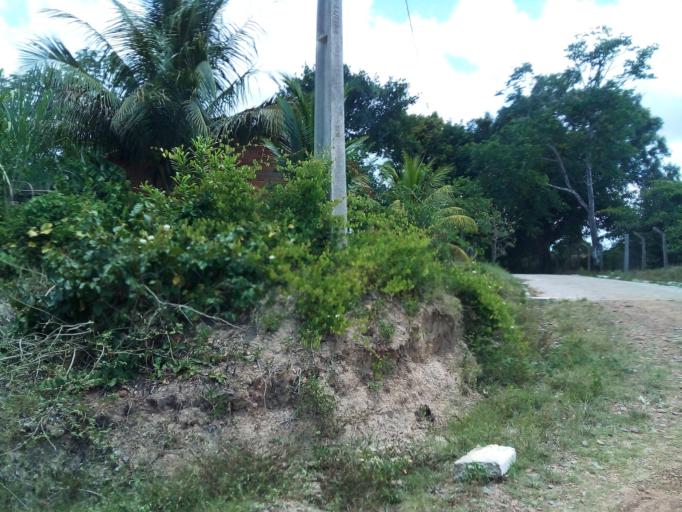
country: BR
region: Maranhao
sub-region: Itapecuru Mirim
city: Itapecuru Mirim
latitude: -3.0432
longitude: -44.3458
